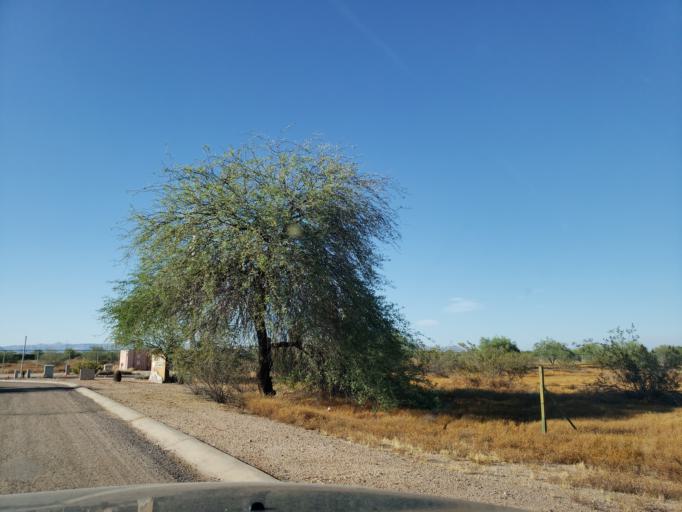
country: US
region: Arizona
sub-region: Maricopa County
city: Cave Creek
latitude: 33.6940
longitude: -112.0249
